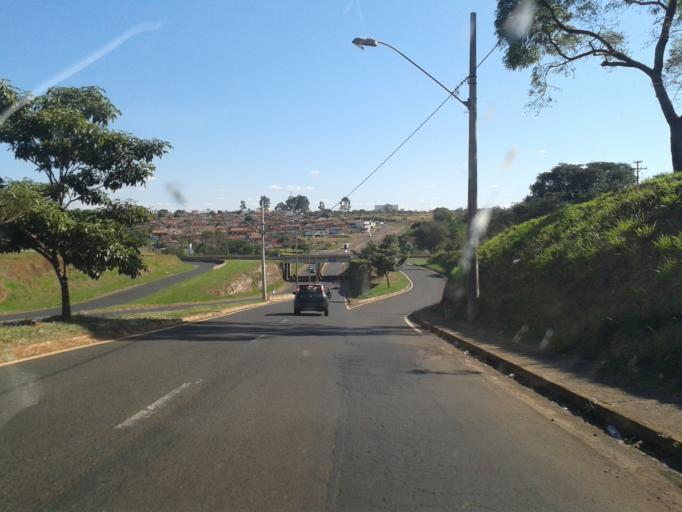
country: BR
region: Minas Gerais
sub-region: Uberaba
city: Uberaba
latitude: -19.7504
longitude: -47.9799
